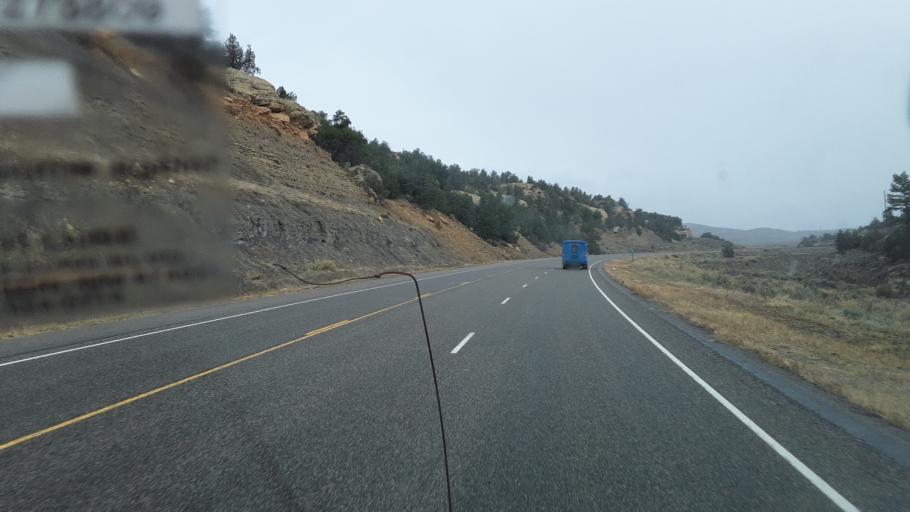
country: US
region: New Mexico
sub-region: Rio Arriba County
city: Tierra Amarilla
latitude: 36.4294
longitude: -106.4783
